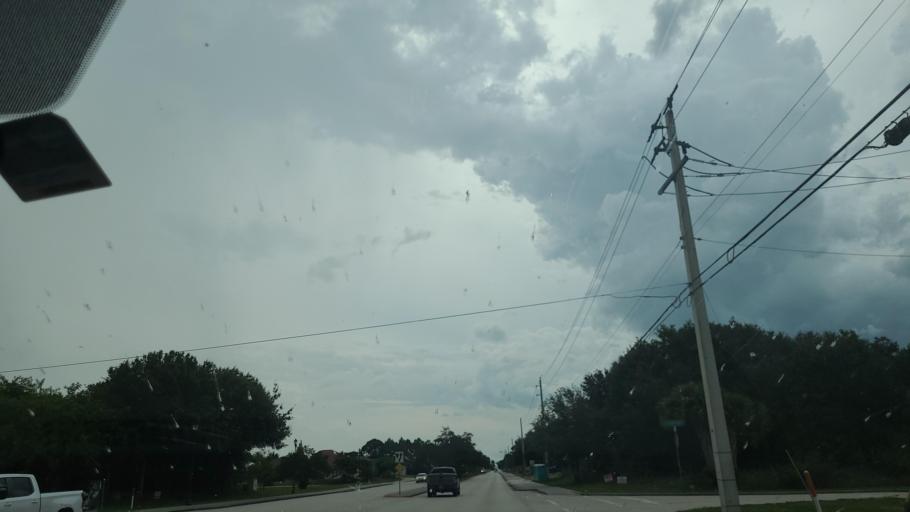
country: US
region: Florida
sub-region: Saint Lucie County
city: Port Saint Lucie
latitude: 27.2098
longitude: -80.3867
